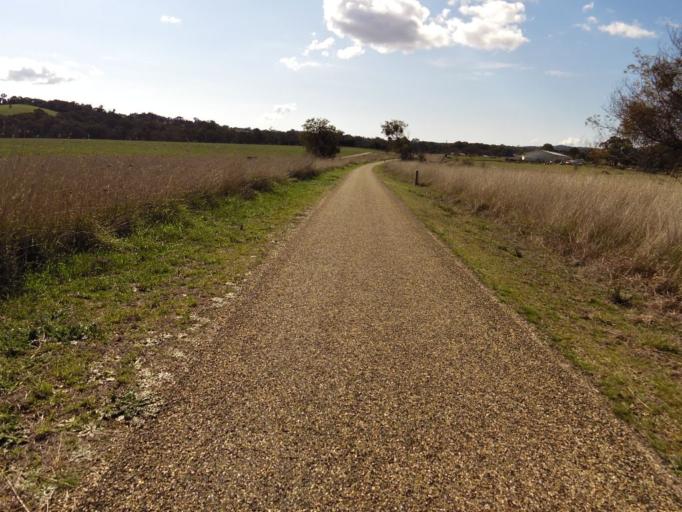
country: AU
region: Victoria
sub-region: Wangaratta
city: Wangaratta
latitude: -36.3965
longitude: 146.6535
